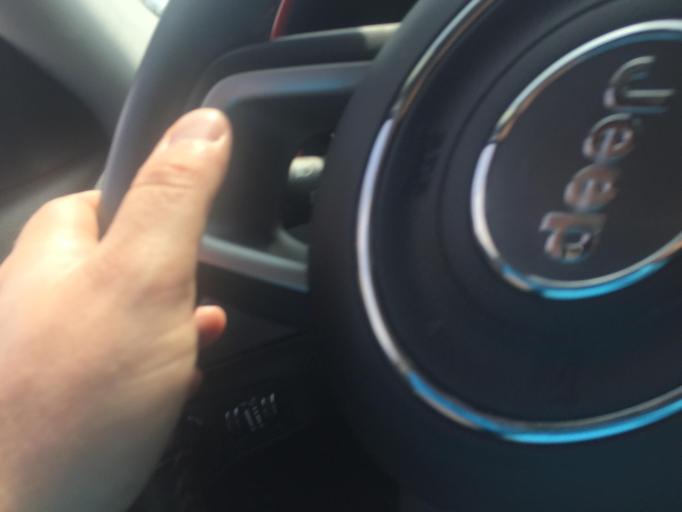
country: US
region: Hawaii
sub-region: Hawaii County
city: Honaunau-Napoopoo
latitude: 19.4248
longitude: -155.9098
